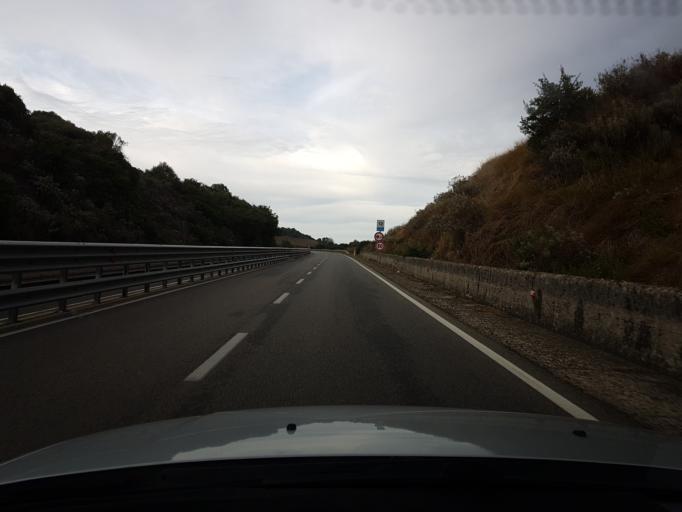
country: IT
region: Sardinia
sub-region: Provincia di Oristano
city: Sedilo
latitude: 40.1598
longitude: 8.9119
